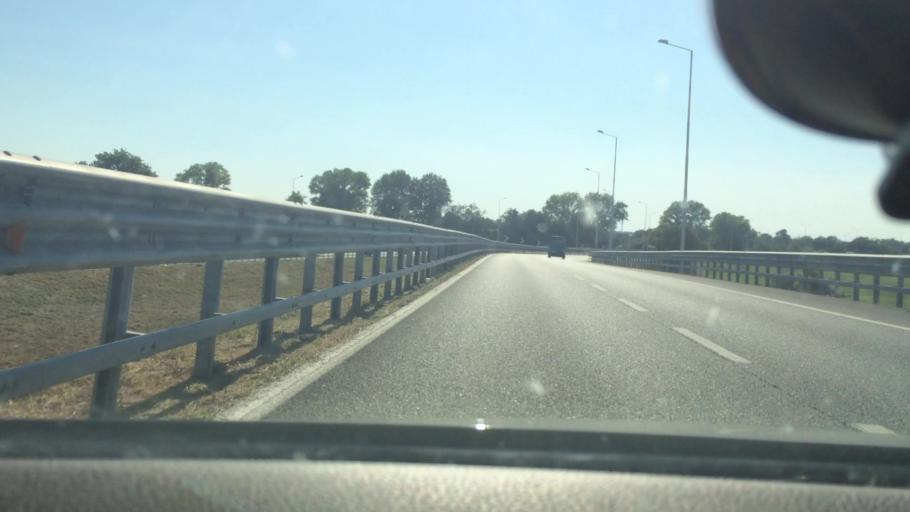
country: IT
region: Lombardy
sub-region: Citta metropolitana di Milano
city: Civesio
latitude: 45.3789
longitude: 9.2742
